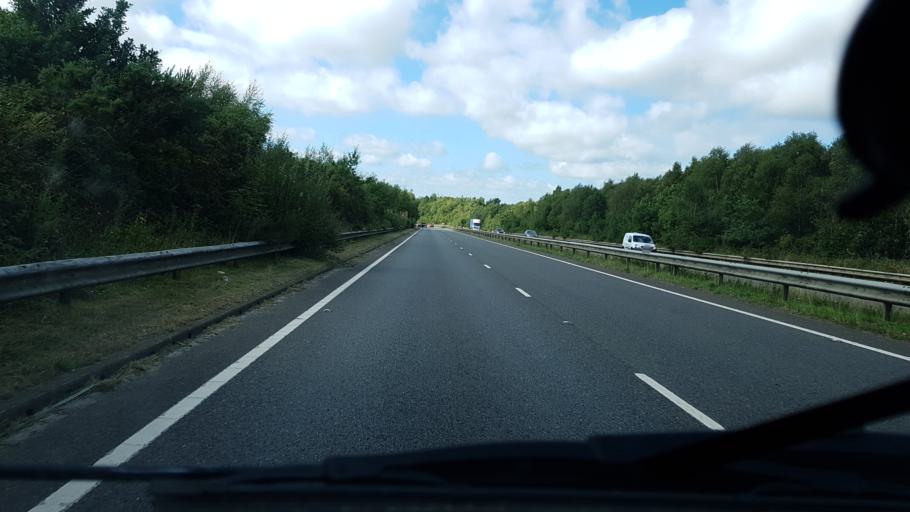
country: GB
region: England
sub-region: West Sussex
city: Broadfield
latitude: 51.0918
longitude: -0.2122
